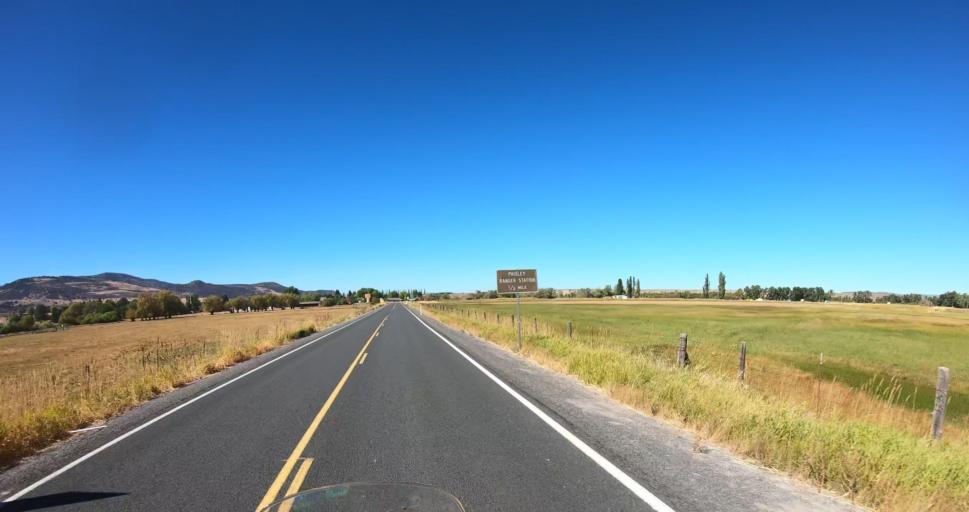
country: US
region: Oregon
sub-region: Lake County
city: Lakeview
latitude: 42.6906
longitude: -120.5347
